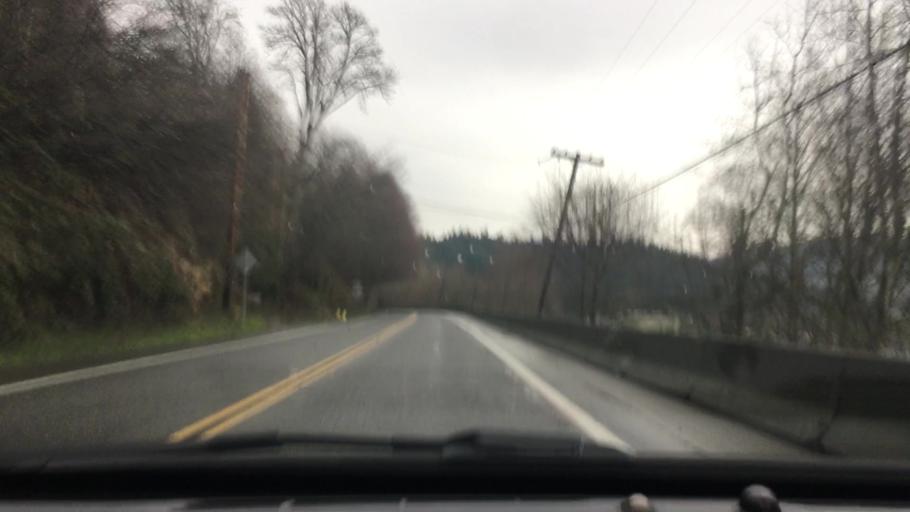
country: US
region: Washington
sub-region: King County
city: West Lake Sammamish
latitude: 47.5695
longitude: -122.0629
